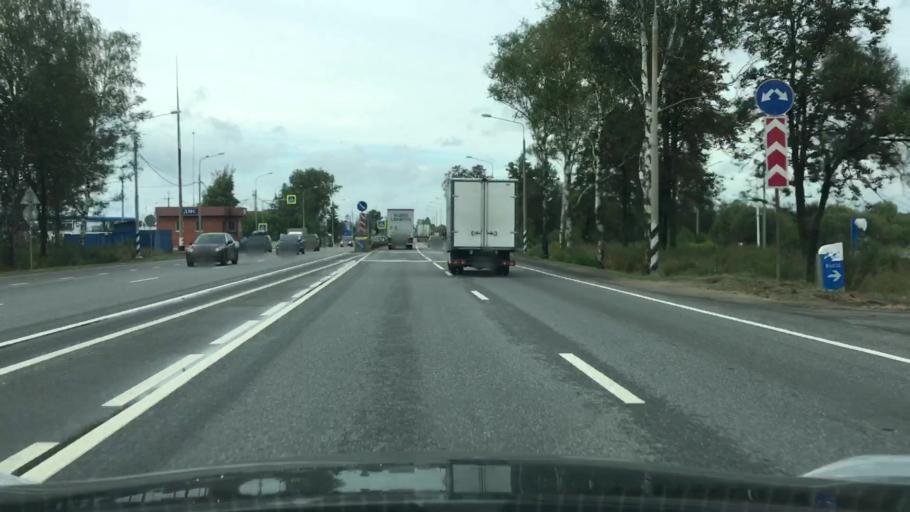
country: RU
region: Moskovskaya
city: Spas-Zaulok
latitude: 56.4912
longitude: 36.5609
